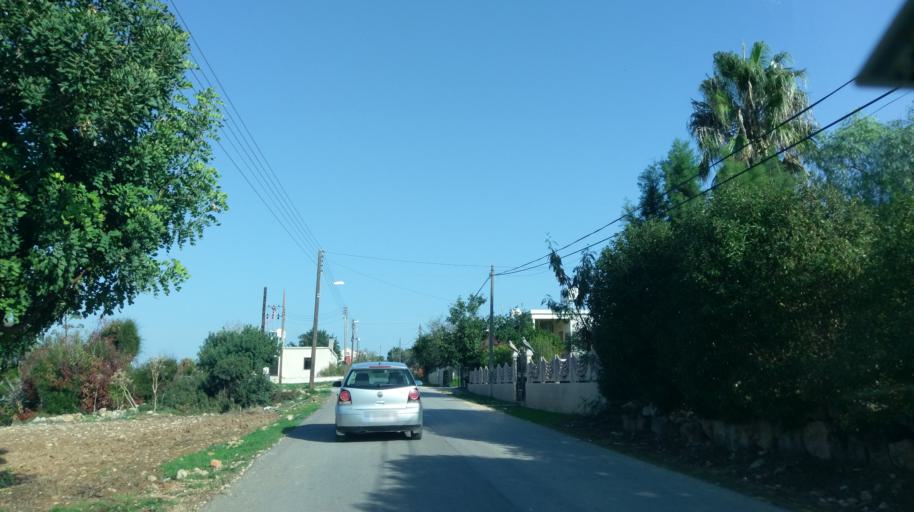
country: CY
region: Ammochostos
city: Leonarisso
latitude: 35.5351
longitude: 34.1960
